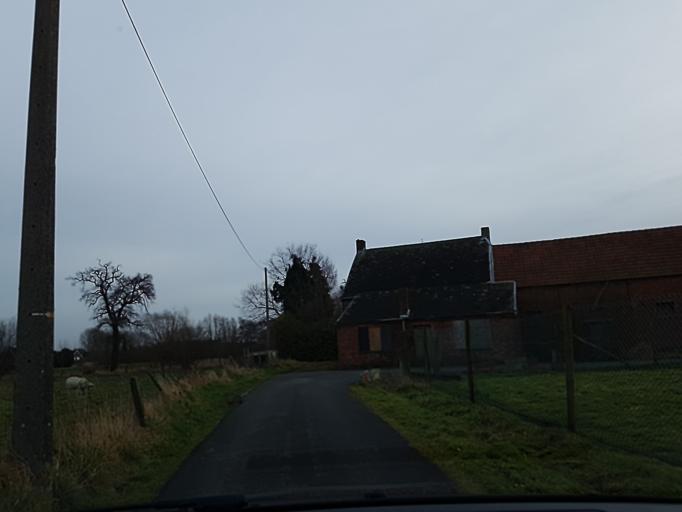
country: BE
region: Flanders
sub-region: Provincie Antwerpen
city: Putte
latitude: 51.0489
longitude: 4.6282
